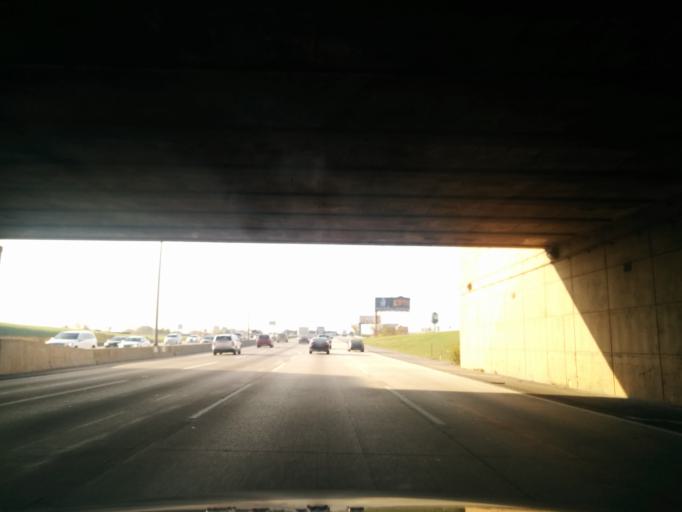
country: US
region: Illinois
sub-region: Cook County
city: Schiller Park
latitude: 41.9509
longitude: -87.8829
